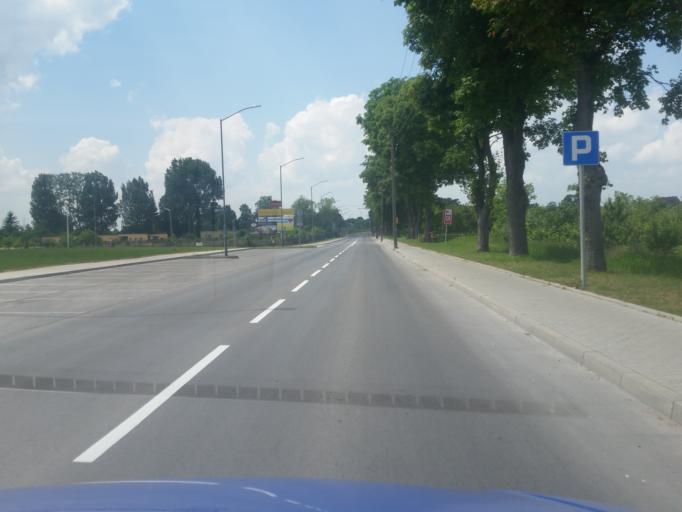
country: PL
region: Swietokrzyskie
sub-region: Powiat buski
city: Busko-Zdroj
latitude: 50.4611
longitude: 20.7052
